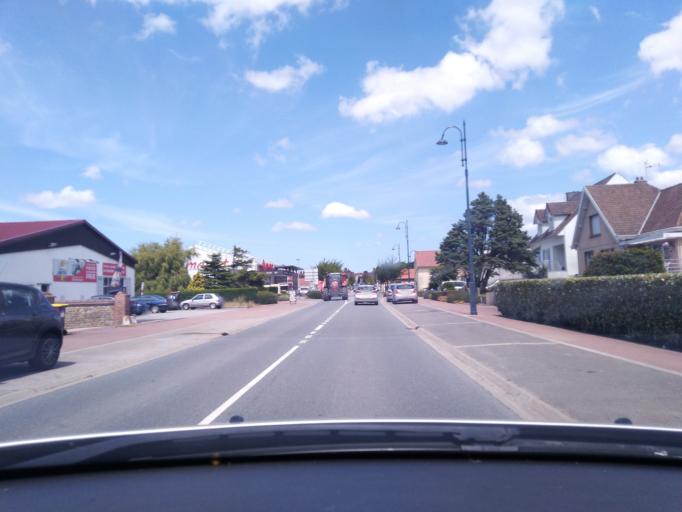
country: FR
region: Nord-Pas-de-Calais
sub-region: Departement du Pas-de-Calais
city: Marquise
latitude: 50.8117
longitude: 1.6983
